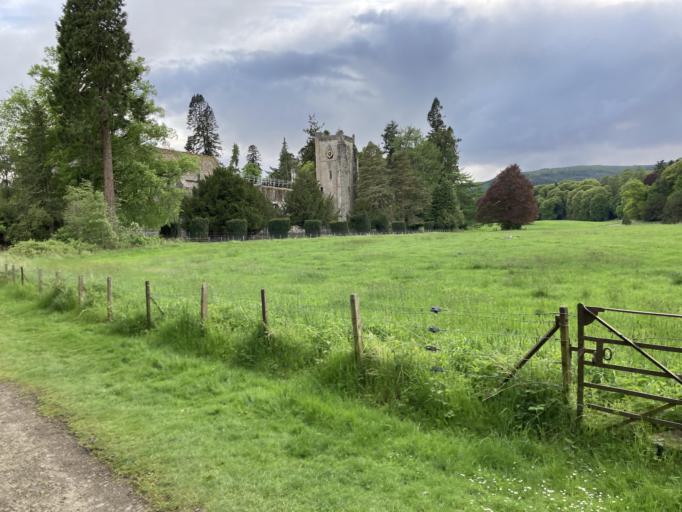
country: GB
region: Scotland
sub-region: Perth and Kinross
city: Bankfoot
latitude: 56.5658
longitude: -3.5882
